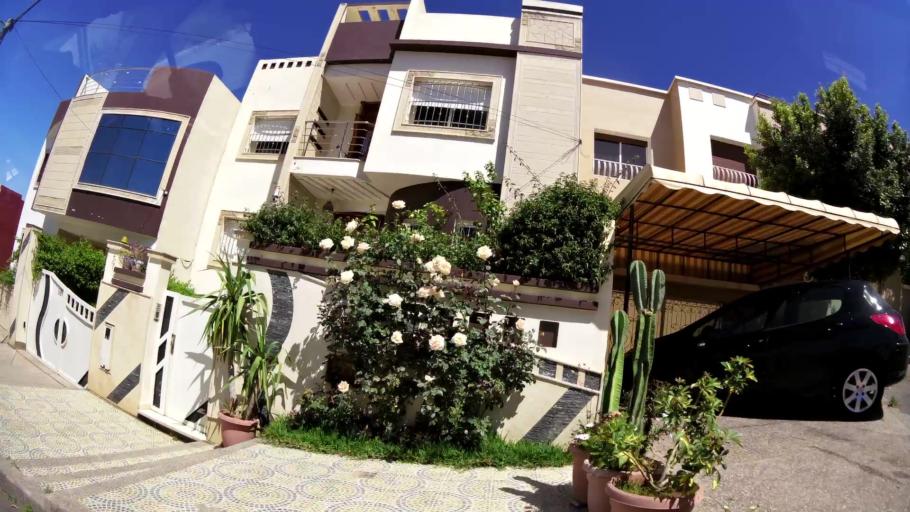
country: MA
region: Oriental
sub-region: Oujda-Angad
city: Oujda
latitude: 34.6464
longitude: -1.9041
